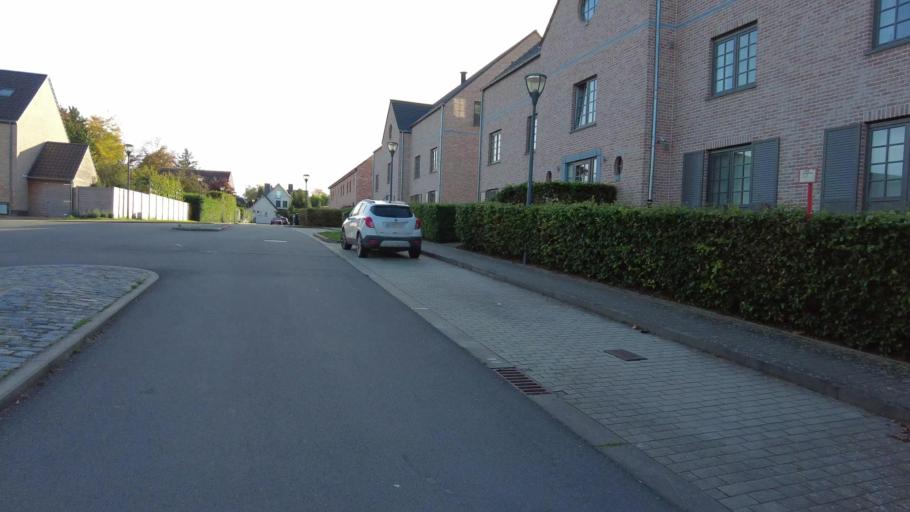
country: BE
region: Wallonia
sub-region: Province du Brabant Wallon
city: Jodoigne
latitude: 50.7205
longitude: 4.8740
